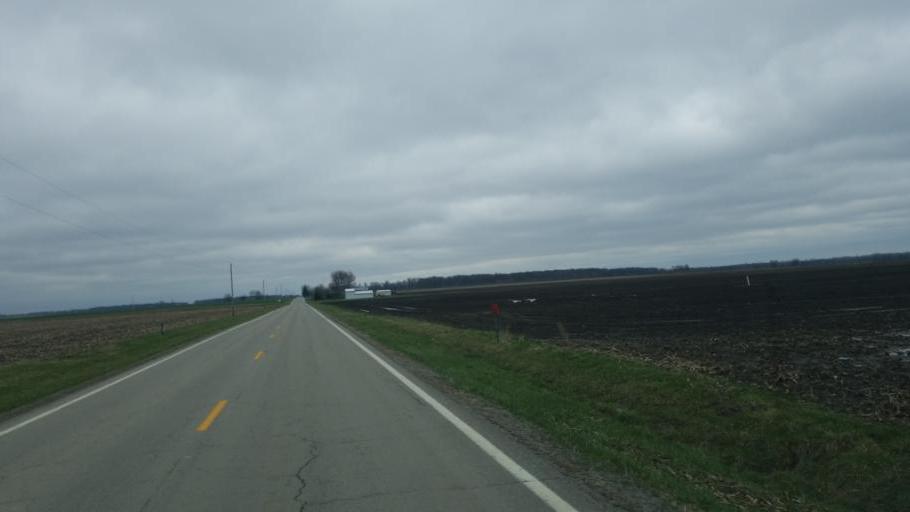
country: US
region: Ohio
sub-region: Wyandot County
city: Upper Sandusky
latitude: 40.7379
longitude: -83.3097
